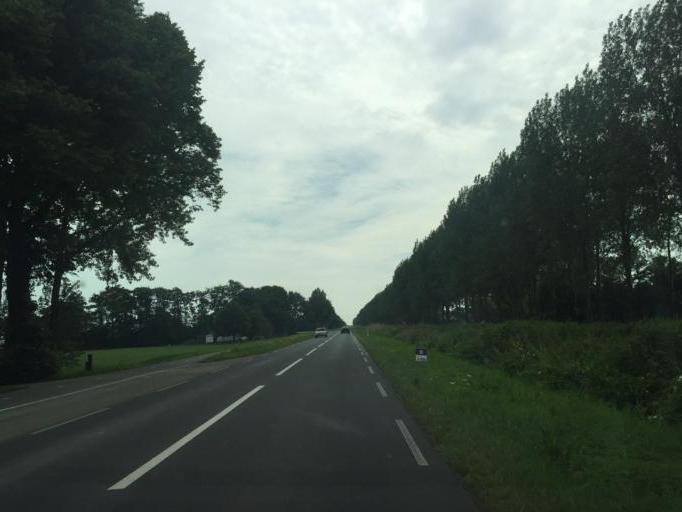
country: NL
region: North Holland
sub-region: Gemeente Heerhugowaard
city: Heerhugowaard
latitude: 52.6093
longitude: 4.8321
